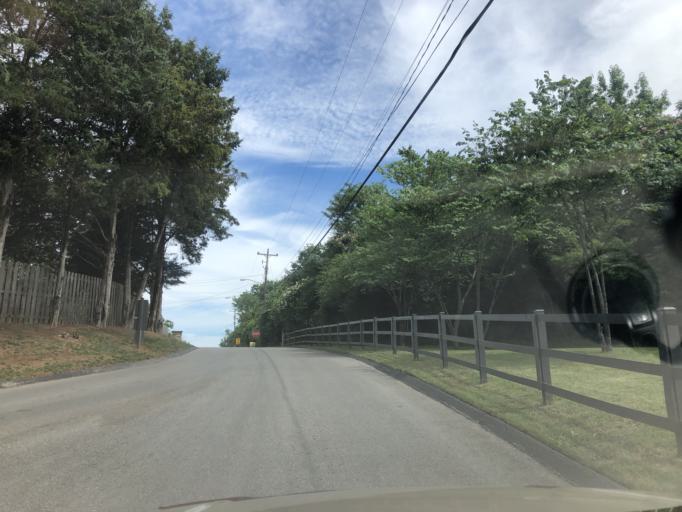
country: US
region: Tennessee
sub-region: Davidson County
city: Lakewood
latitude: 36.2575
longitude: -86.6209
